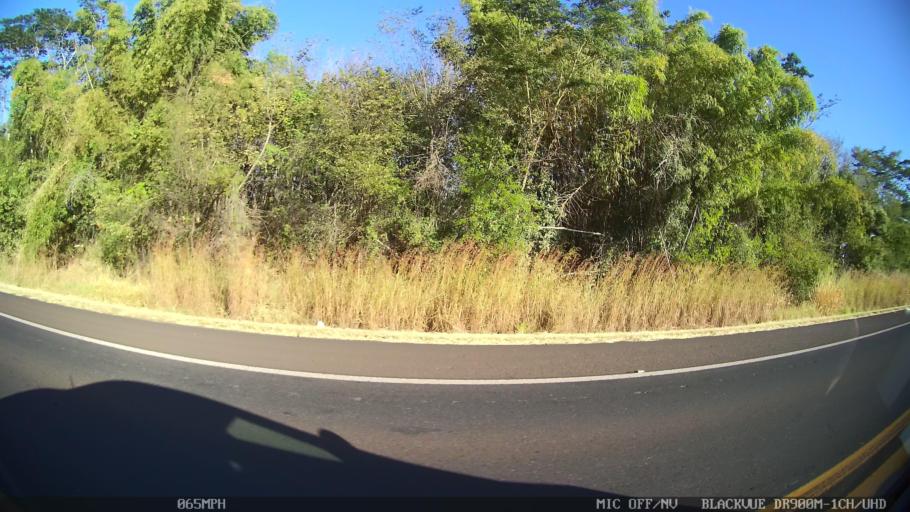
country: BR
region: Sao Paulo
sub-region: Olimpia
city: Olimpia
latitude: -20.7128
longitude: -48.9840
